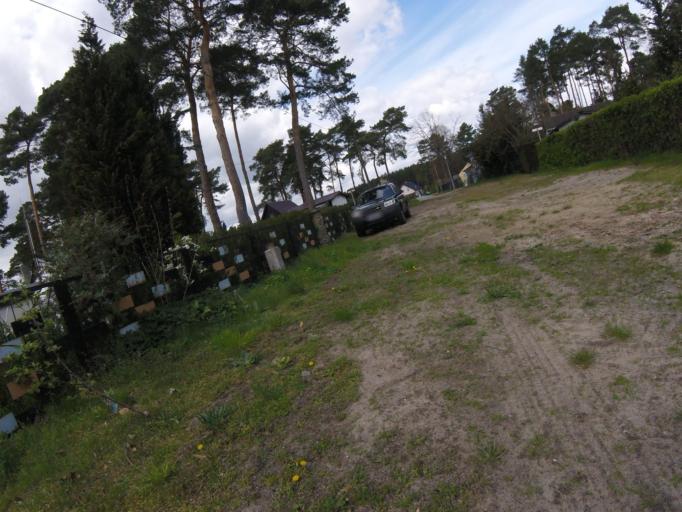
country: DE
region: Brandenburg
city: Bestensee
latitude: 52.2282
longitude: 13.6406
